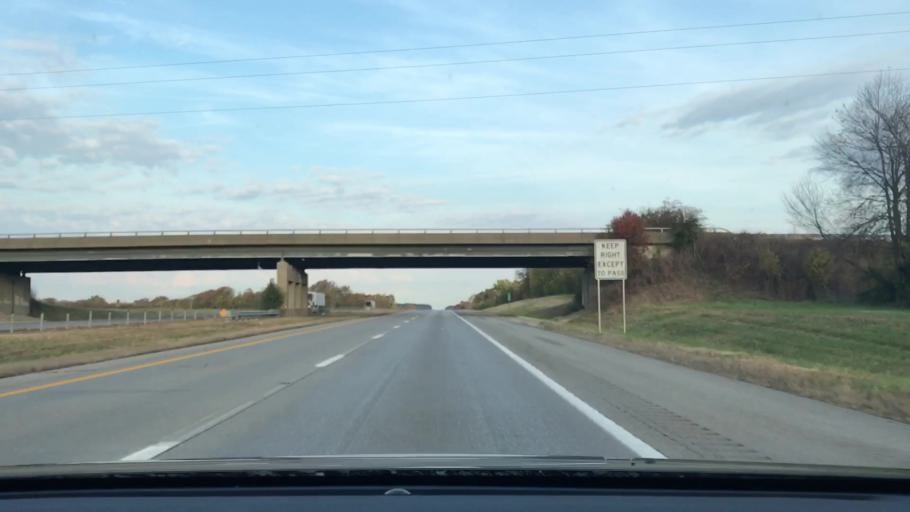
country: US
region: Kentucky
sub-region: Christian County
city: Hopkinsville
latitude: 36.7544
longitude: -87.5285
